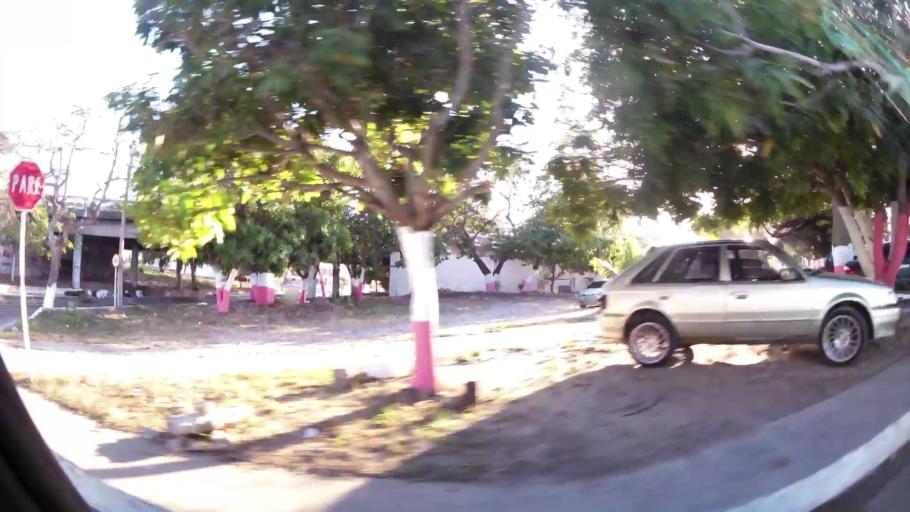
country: CO
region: Atlantico
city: Barranquilla
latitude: 10.9837
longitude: -74.8020
